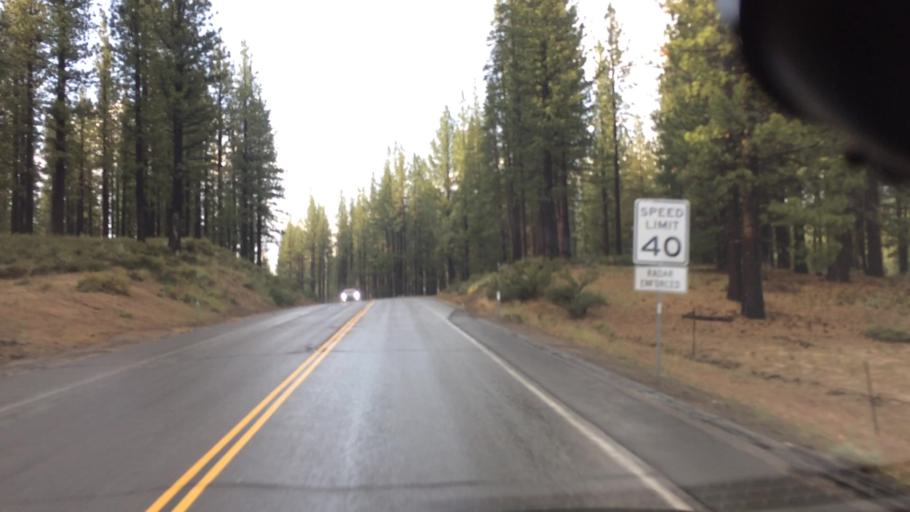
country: US
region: California
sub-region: El Dorado County
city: South Lake Tahoe
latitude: 38.8998
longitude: -119.9699
